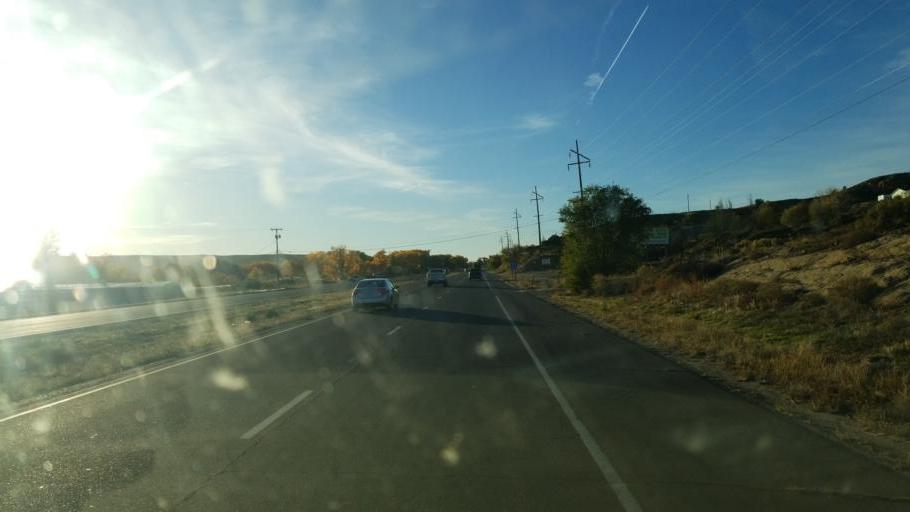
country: US
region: New Mexico
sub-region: San Juan County
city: Lee Acres
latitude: 36.7069
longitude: -108.1208
